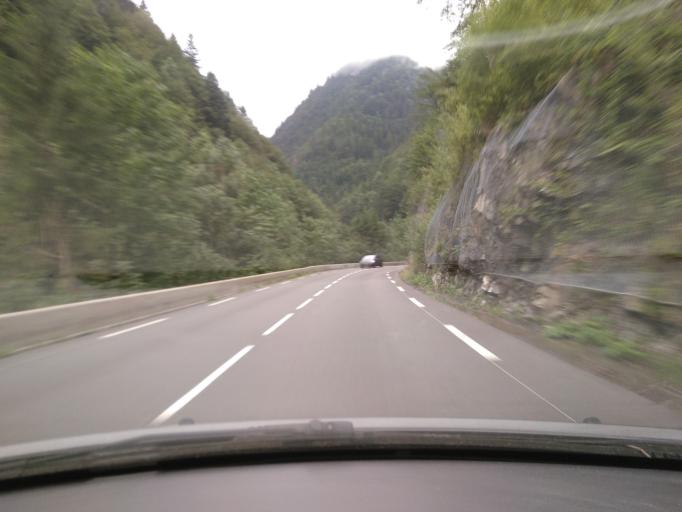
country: FR
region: Rhone-Alpes
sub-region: Departement de la Haute-Savoie
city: Saint-Jean-de-Sixt
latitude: 45.9403
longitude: 6.4021
